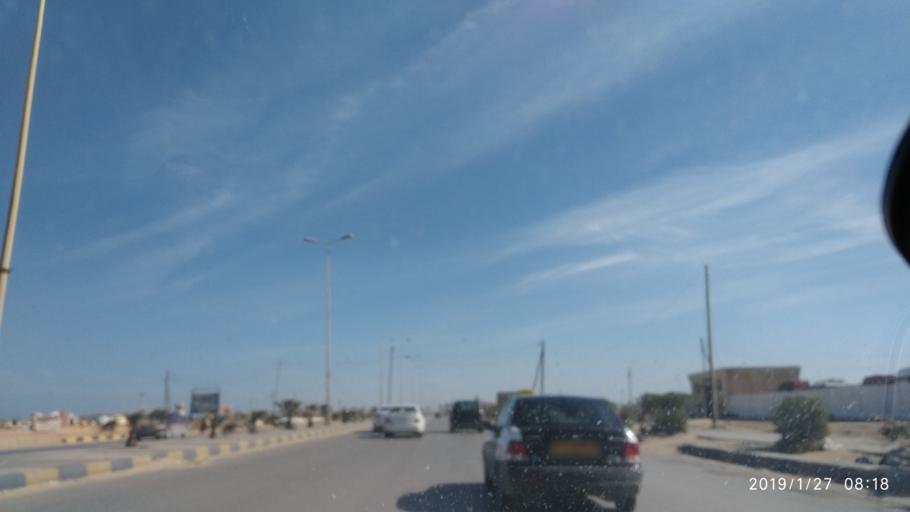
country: LY
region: Tripoli
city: Tagiura
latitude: 32.8955
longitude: 13.3267
